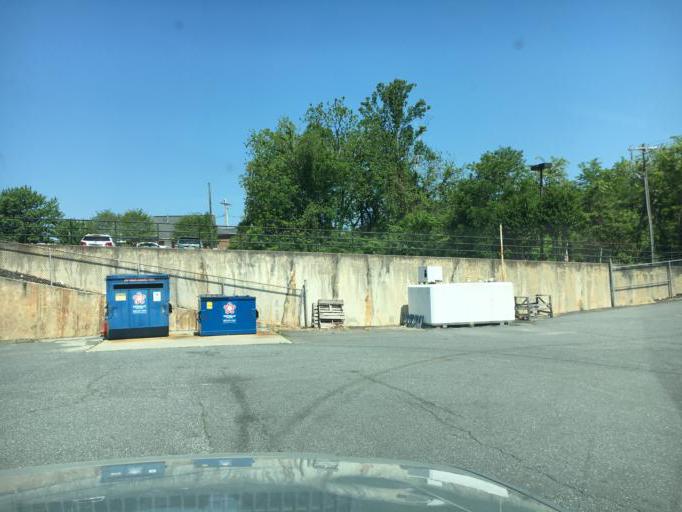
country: US
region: North Carolina
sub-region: Burke County
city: Morganton
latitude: 35.7446
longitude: -81.6835
